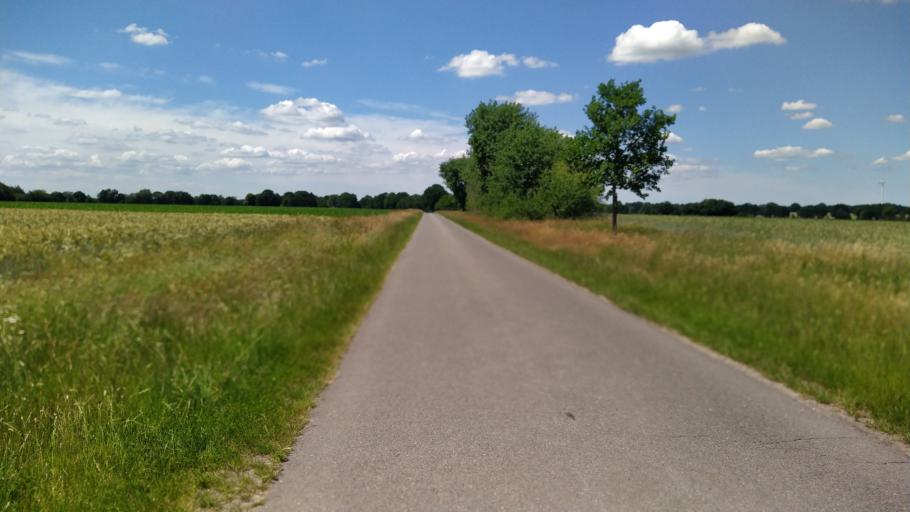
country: DE
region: Lower Saxony
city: Estorf
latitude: 53.5606
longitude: 9.2245
